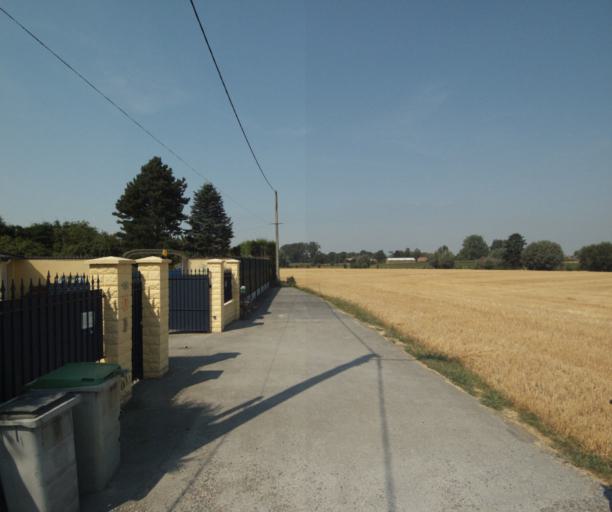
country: FR
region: Nord-Pas-de-Calais
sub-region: Departement du Nord
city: Quesnoy-sur-Deule
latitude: 50.7108
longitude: 3.0180
